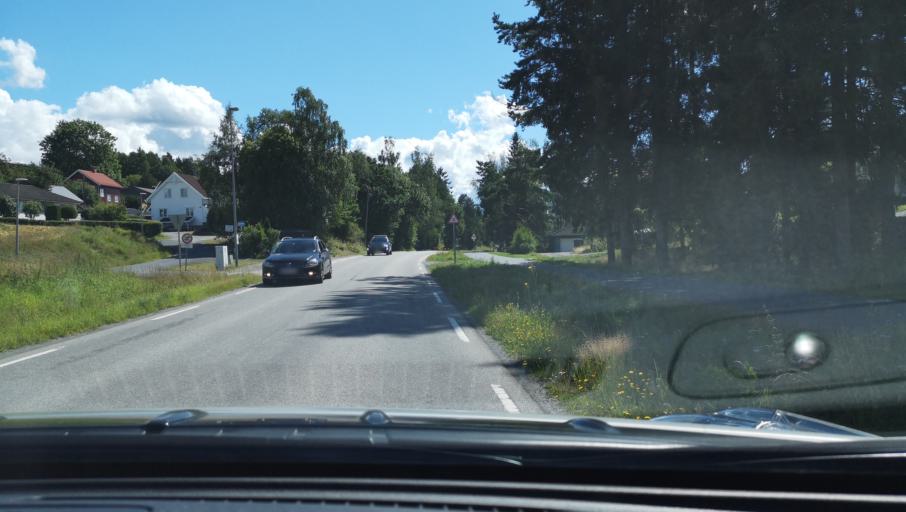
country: NO
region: Akershus
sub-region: As
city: As
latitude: 59.6556
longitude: 10.7998
